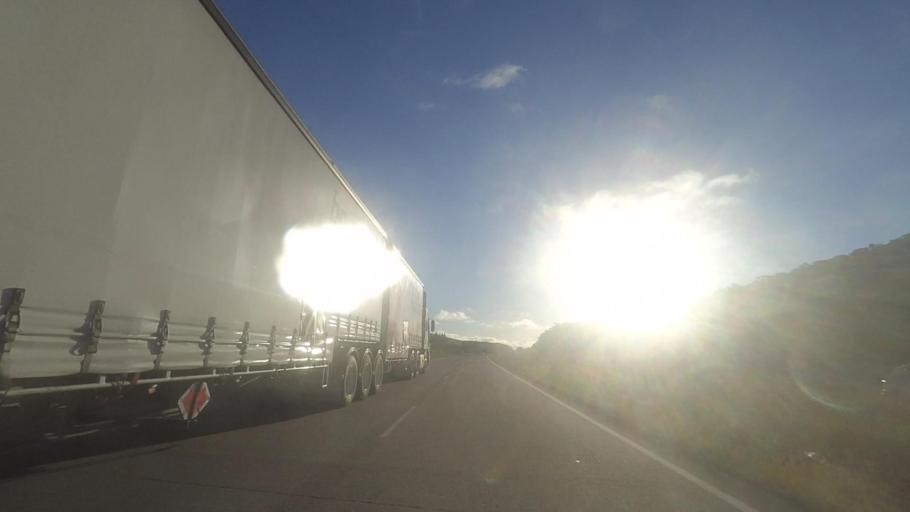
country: AU
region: New South Wales
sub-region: Great Lakes
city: Bulahdelah
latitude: -32.5207
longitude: 152.2041
